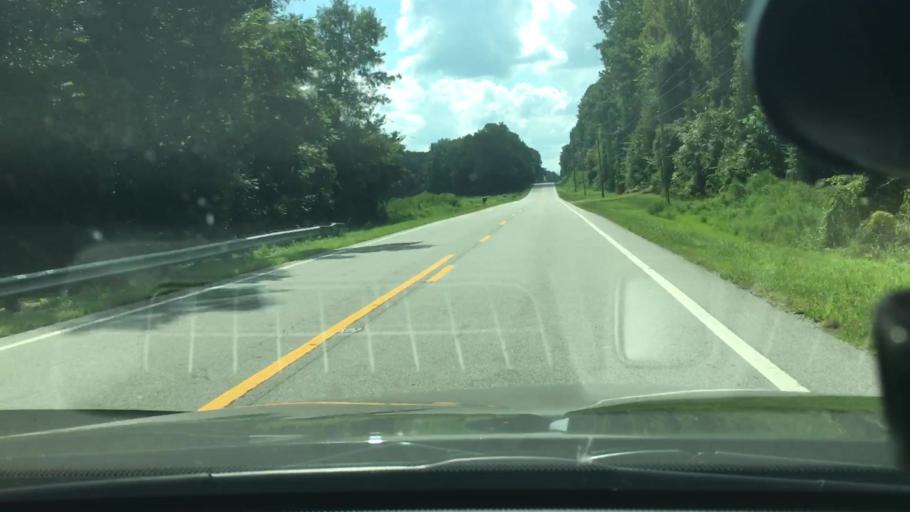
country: US
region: North Carolina
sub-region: Pitt County
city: Farmville
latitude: 35.6907
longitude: -77.4968
